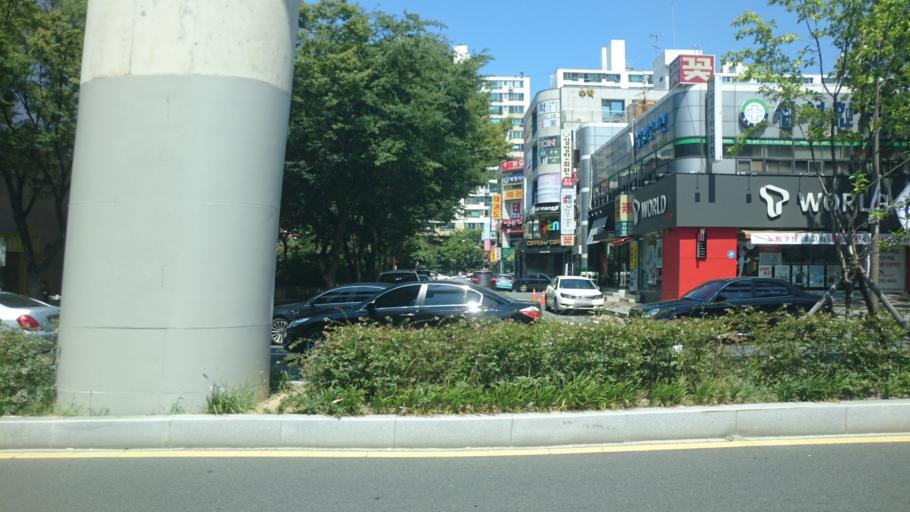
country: KR
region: Daegu
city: Daegu
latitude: 35.8205
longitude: 128.6404
